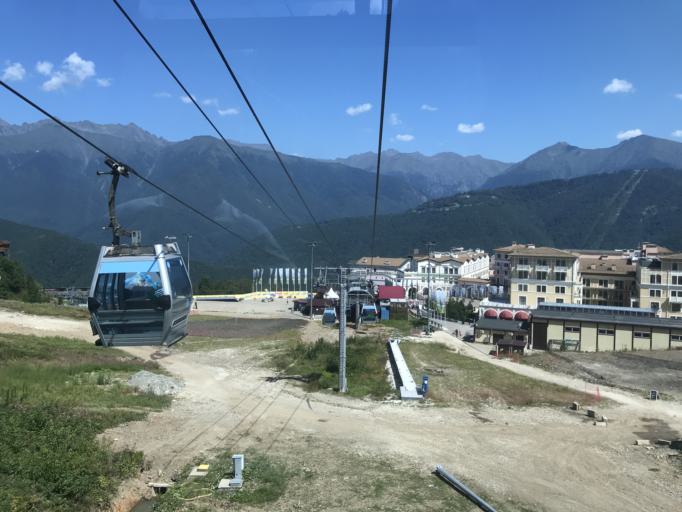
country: RU
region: Krasnodarskiy
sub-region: Sochi City
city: Krasnaya Polyana
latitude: 43.6674
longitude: 40.2579
